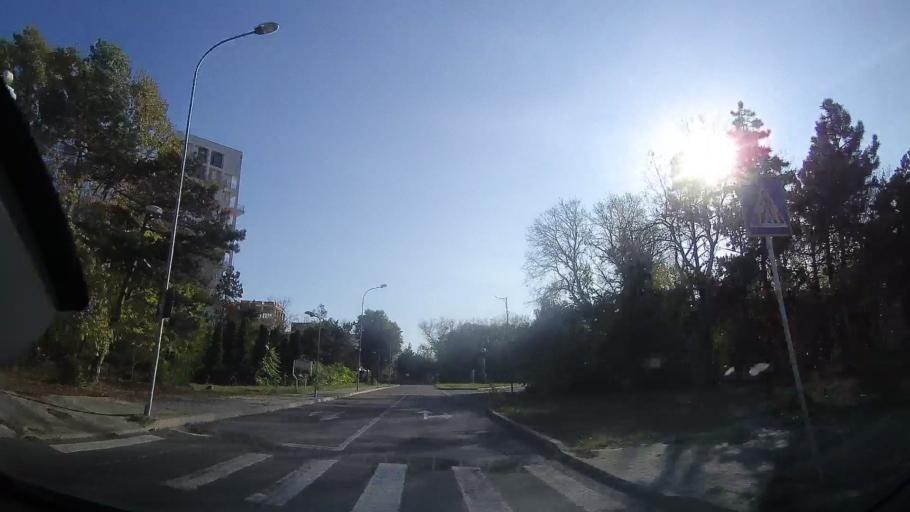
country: RO
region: Constanta
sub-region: Comuna Douazeci si Trei August
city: Douazeci si Trei August
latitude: 43.8609
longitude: 28.5981
